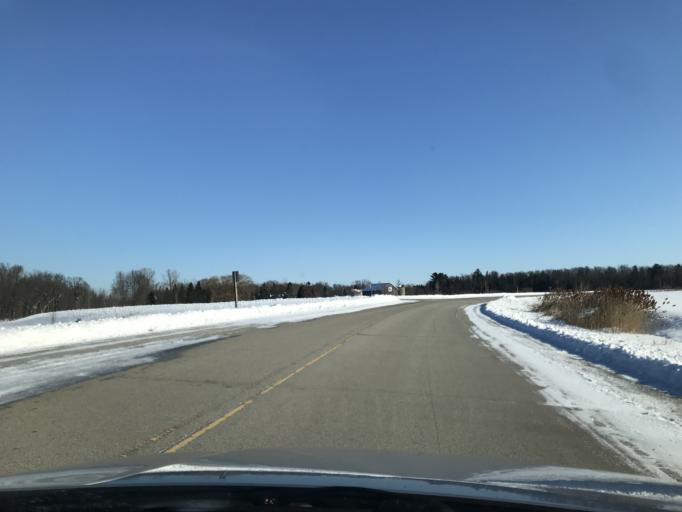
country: US
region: Wisconsin
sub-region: Oconto County
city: Oconto Falls
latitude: 44.9692
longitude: -88.0456
